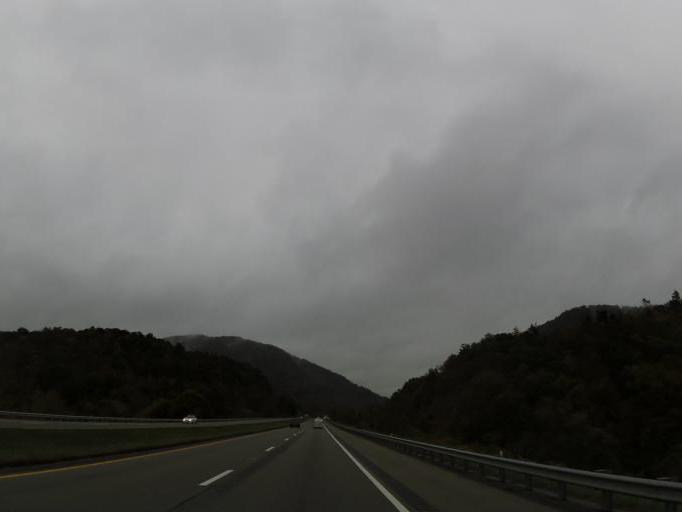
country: US
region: Virginia
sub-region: Wythe County
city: Wytheville
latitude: 37.0012
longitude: -81.0910
